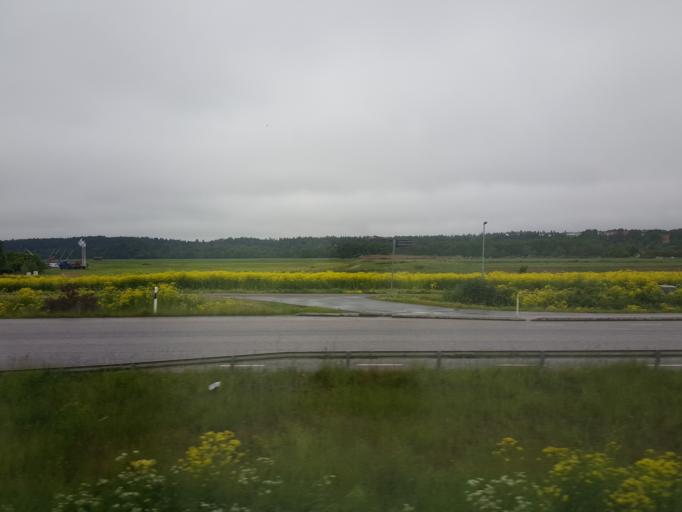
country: SE
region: Uppsala
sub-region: Uppsala Kommun
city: Uppsala
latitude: 59.8450
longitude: 17.6723
